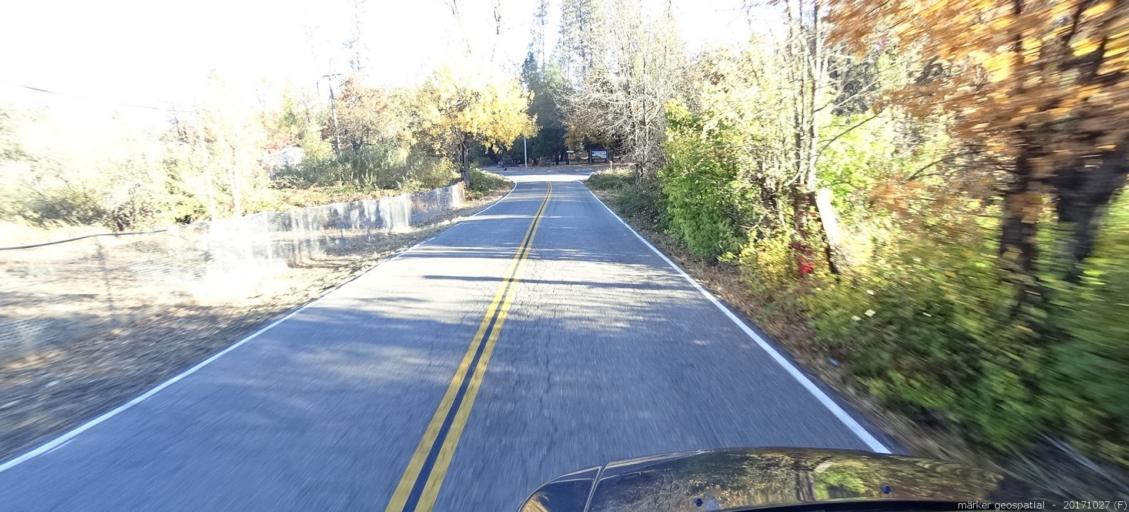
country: US
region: California
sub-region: Shasta County
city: Burney
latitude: 41.0135
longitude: -121.9062
